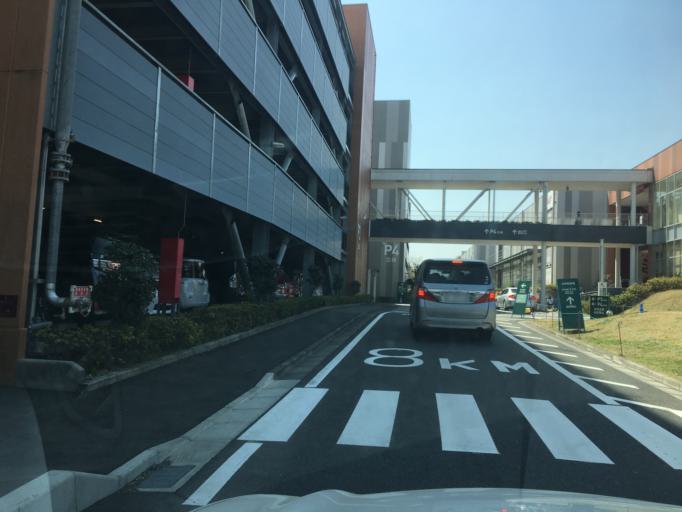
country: JP
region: Saitama
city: Sayama
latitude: 35.8103
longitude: 139.3821
